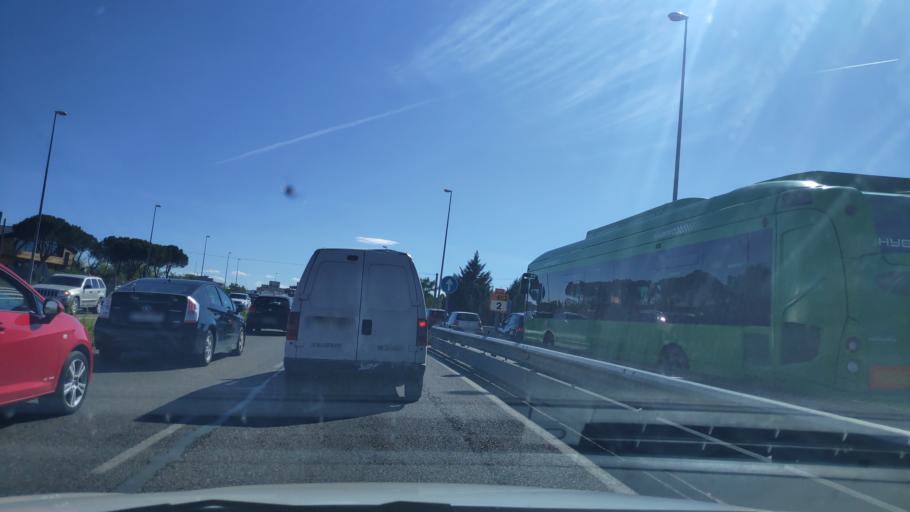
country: ES
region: Madrid
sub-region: Provincia de Madrid
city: Las Tablas
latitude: 40.5188
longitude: -3.6664
